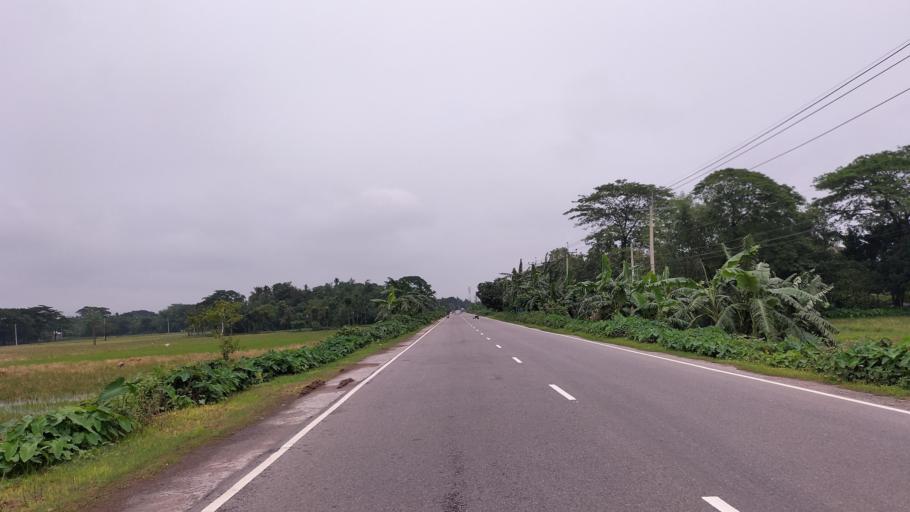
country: BD
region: Dhaka
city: Netrakona
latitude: 24.8508
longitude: 90.6318
